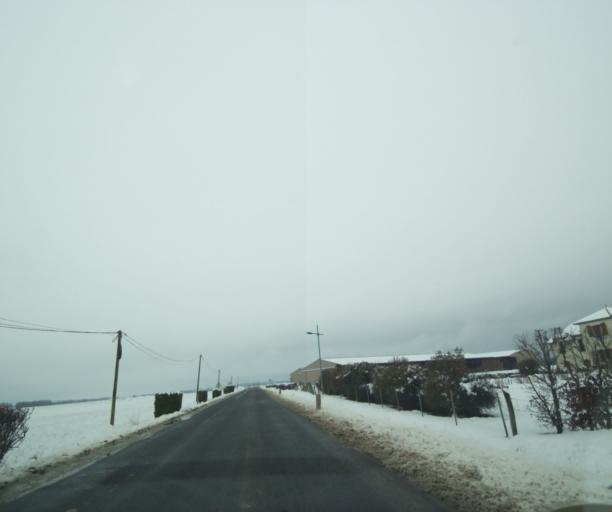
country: FR
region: Champagne-Ardenne
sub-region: Departement de la Haute-Marne
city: Montier-en-Der
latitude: 48.4429
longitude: 4.8028
